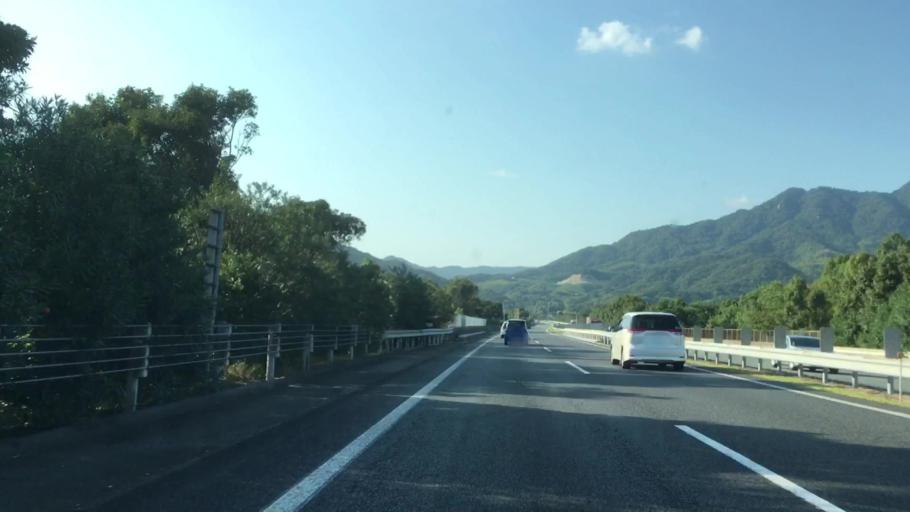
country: JP
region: Yamaguchi
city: Hofu
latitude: 34.0630
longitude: 131.6075
